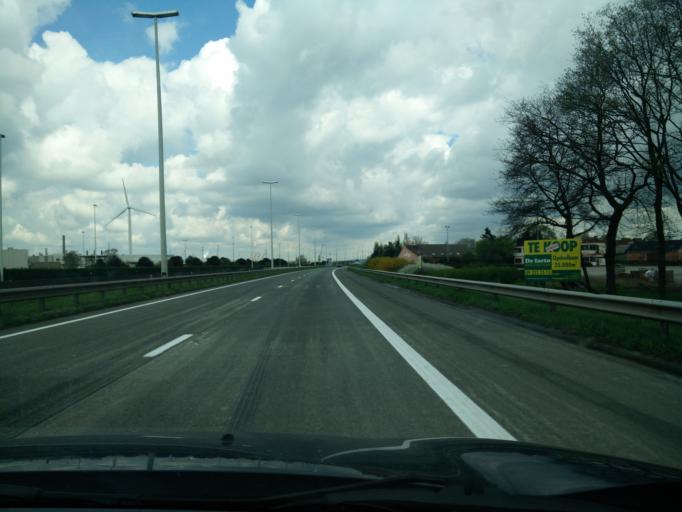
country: BE
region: Flanders
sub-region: Provincie Oost-Vlaanderen
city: Evergem
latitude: 51.0973
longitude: 3.7566
